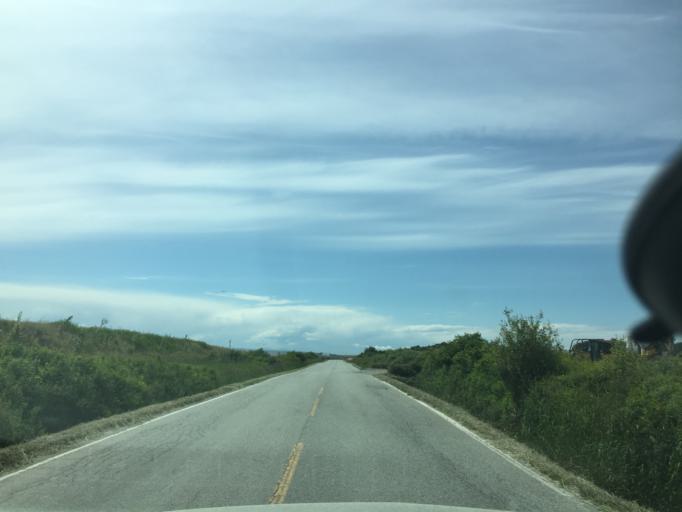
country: CA
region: British Columbia
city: Richmond
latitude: 49.2066
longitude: -123.1877
